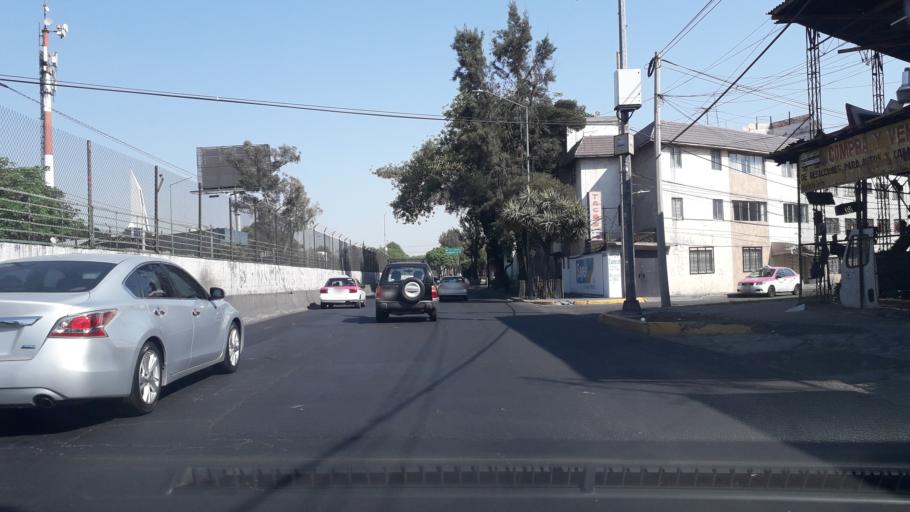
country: MX
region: Mexico City
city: Cuauhtemoc
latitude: 19.4671
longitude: -99.1345
